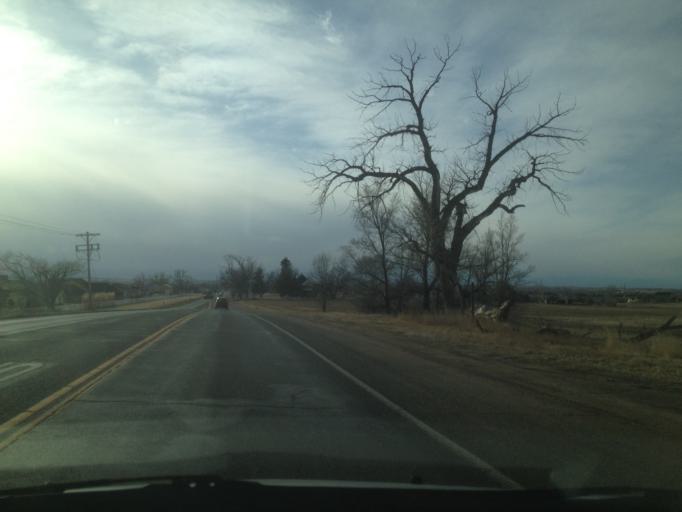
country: US
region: Colorado
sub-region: Weld County
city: Fort Lupton
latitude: 40.0803
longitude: -104.7906
